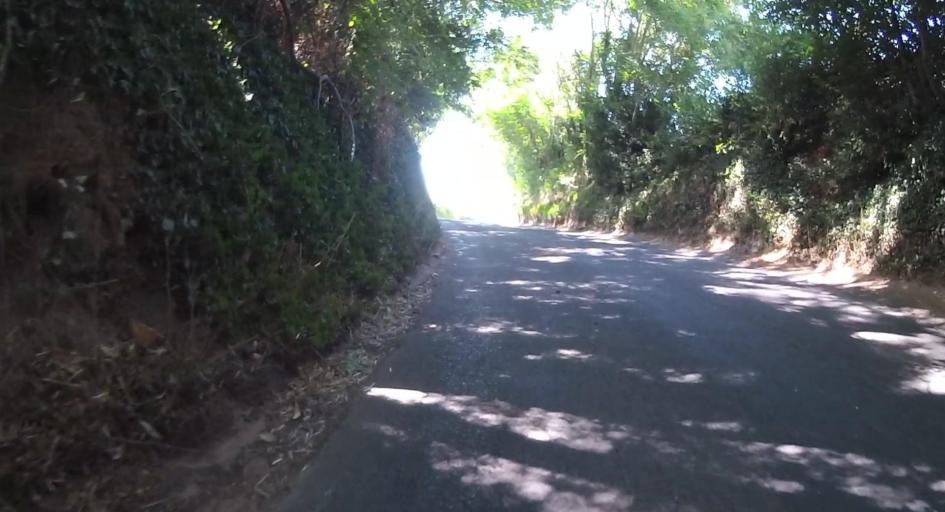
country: GB
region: England
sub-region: Dorset
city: Wareham
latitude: 50.6381
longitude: -2.0637
